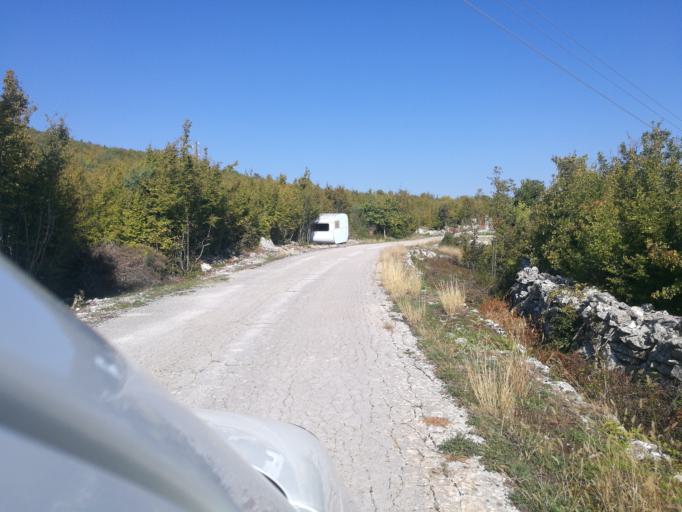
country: HR
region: Splitsko-Dalmatinska
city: Trilj
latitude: 43.5419
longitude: 16.7331
